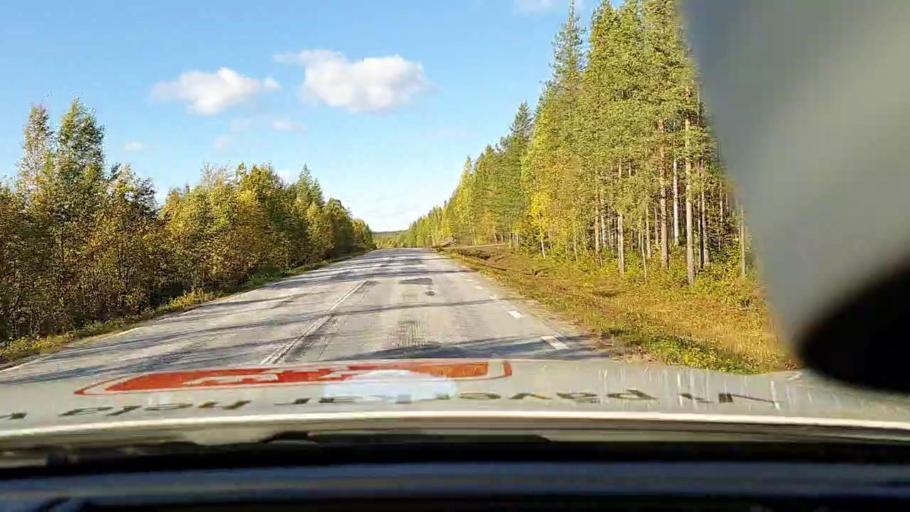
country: SE
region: Norrbotten
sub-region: Pitea Kommun
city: Norrfjarden
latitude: 65.4542
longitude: 21.4560
